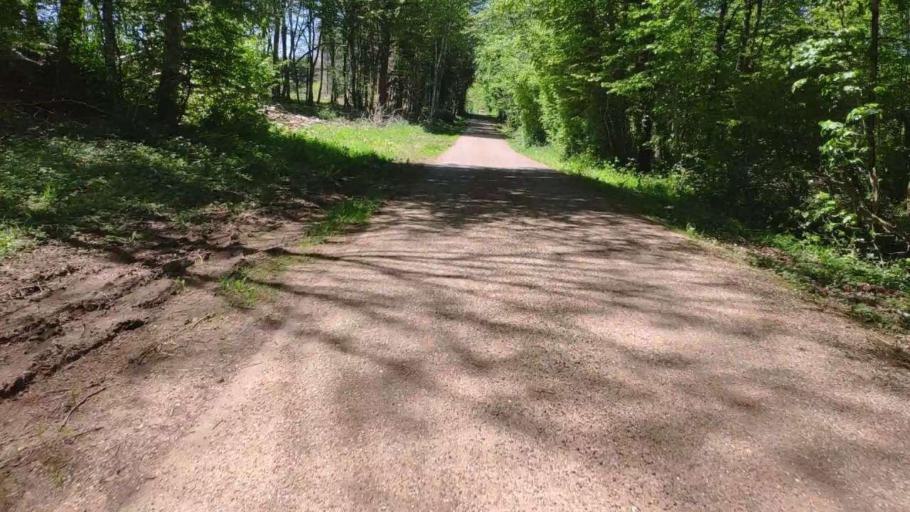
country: FR
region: Franche-Comte
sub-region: Departement du Jura
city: Poligny
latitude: 46.7346
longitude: 5.6725
